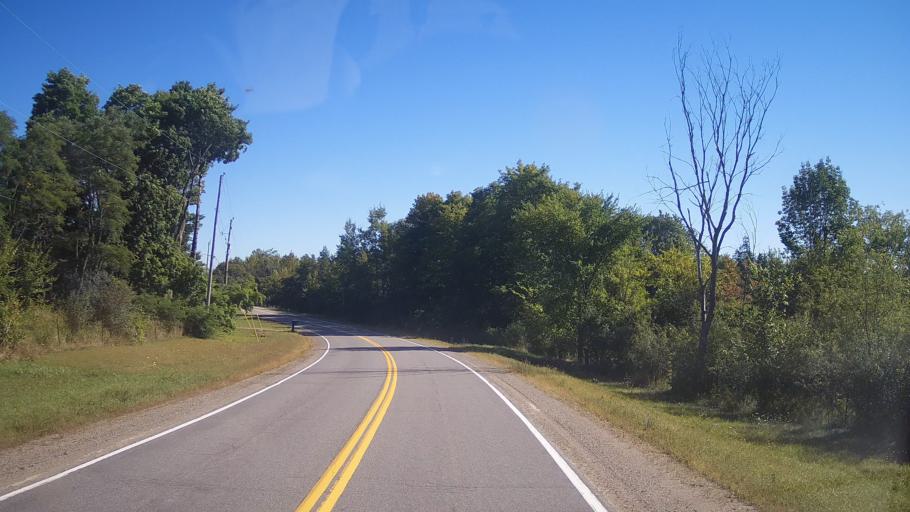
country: CA
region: Ontario
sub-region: Lanark County
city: Smiths Falls
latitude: 44.8042
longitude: -75.9715
